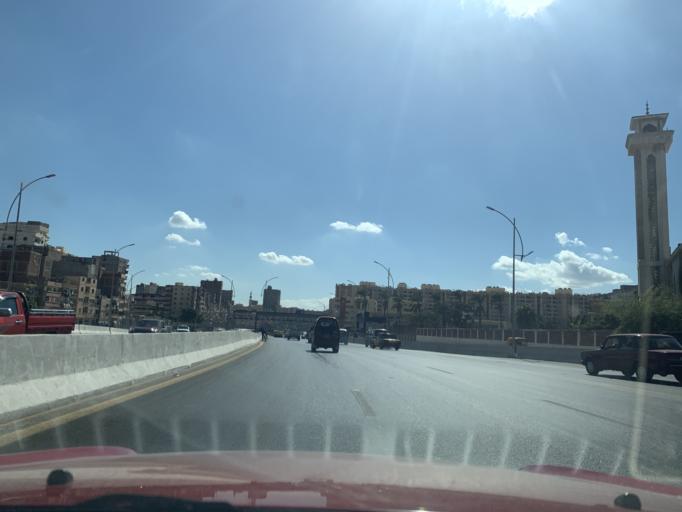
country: EG
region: Alexandria
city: Alexandria
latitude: 31.2197
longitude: 29.9642
